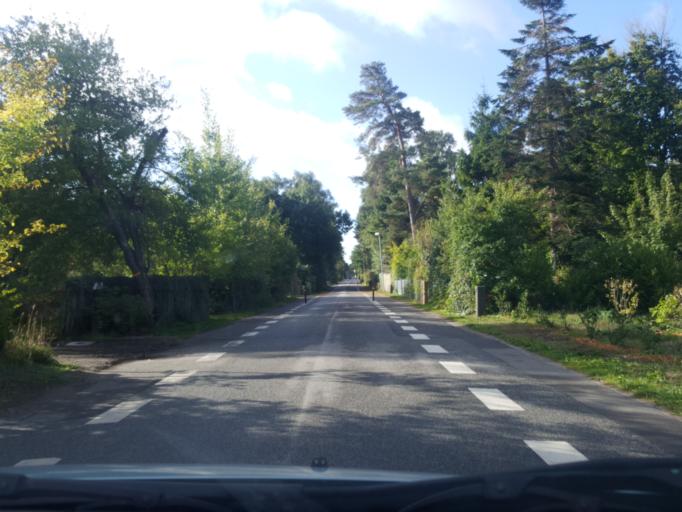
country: DK
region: Zealand
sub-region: Guldborgsund Kommune
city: Nykobing Falster
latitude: 54.6819
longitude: 11.9627
